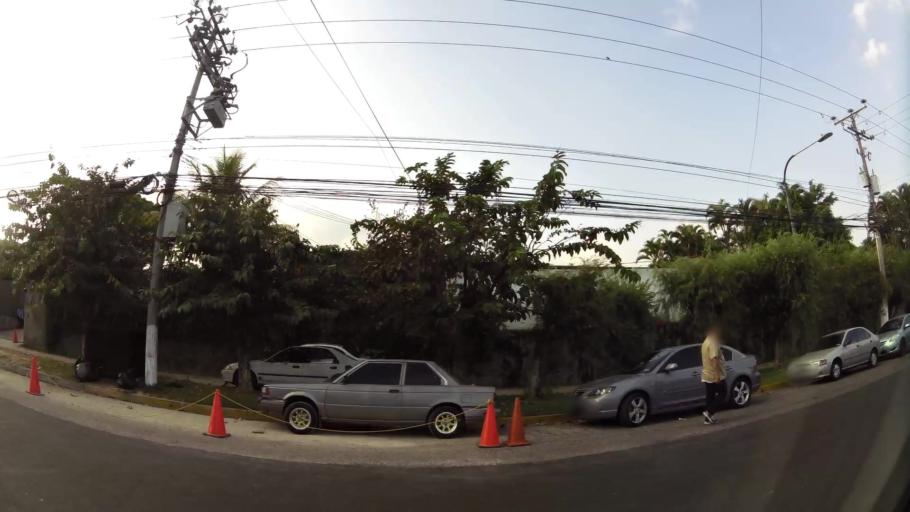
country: SV
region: La Libertad
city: Antiguo Cuscatlan
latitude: 13.6943
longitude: -89.2436
